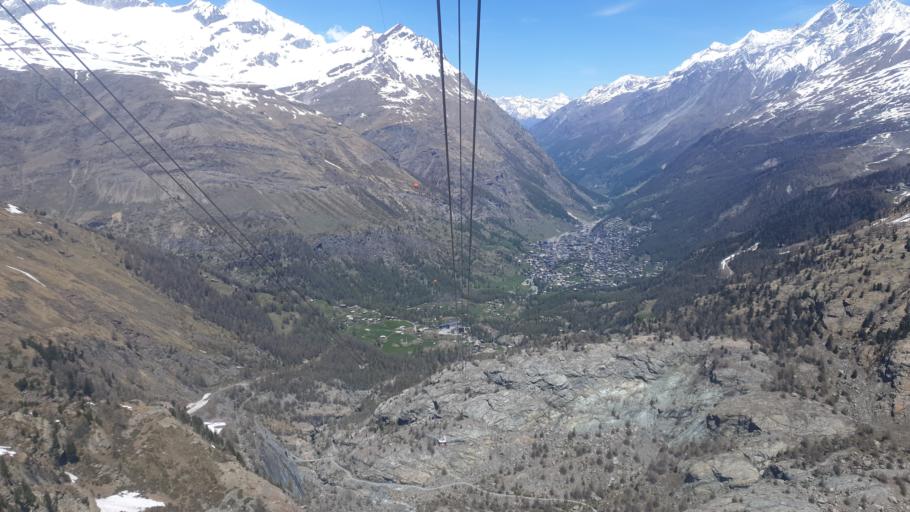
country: CH
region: Valais
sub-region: Visp District
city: Zermatt
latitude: 45.9851
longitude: 7.7268
